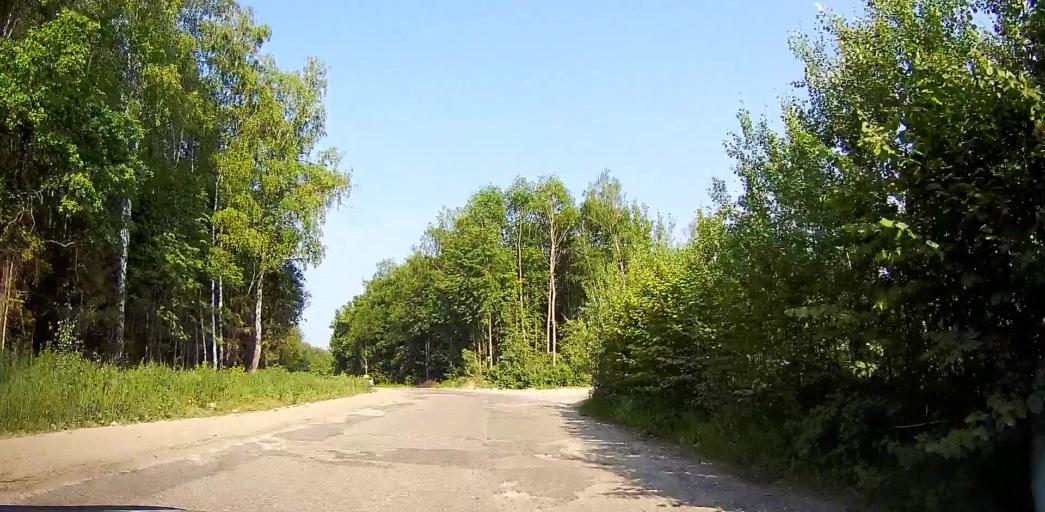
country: RU
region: Moskovskaya
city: Yakovlevskoye
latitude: 55.4308
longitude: 37.9102
